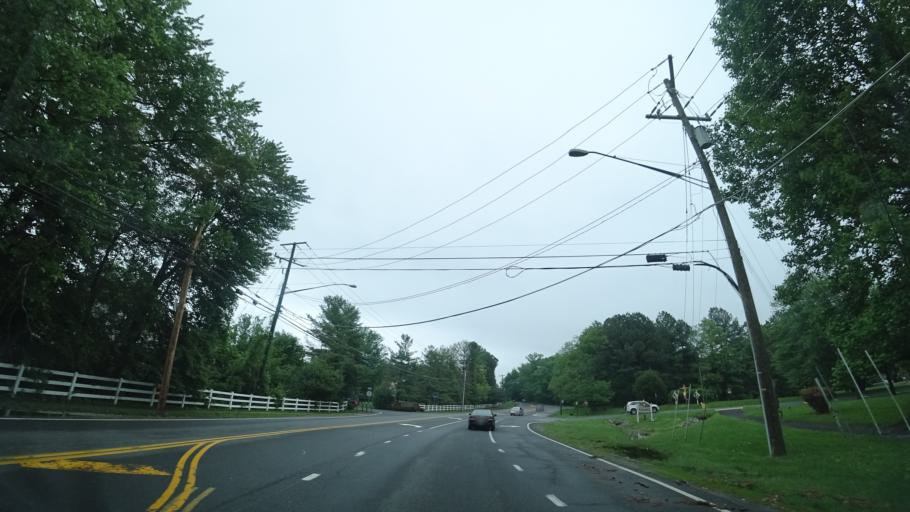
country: US
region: Virginia
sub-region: Fairfax County
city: Tysons Corner
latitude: 38.9375
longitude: -77.2398
